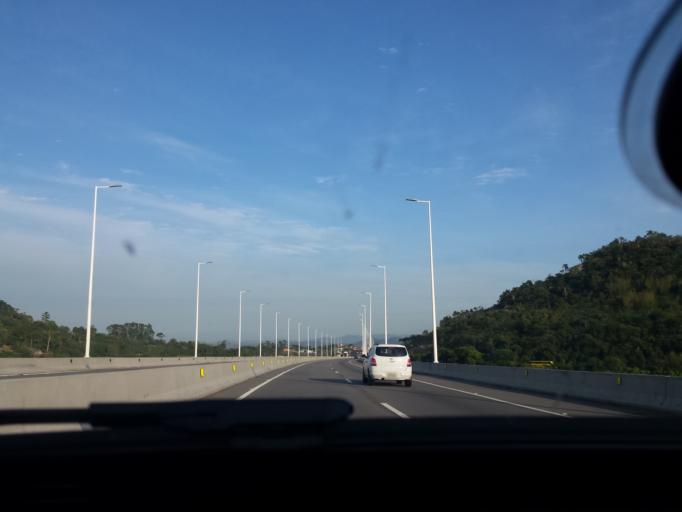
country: BR
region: Santa Catarina
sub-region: Laguna
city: Laguna
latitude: -28.4320
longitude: -48.8474
